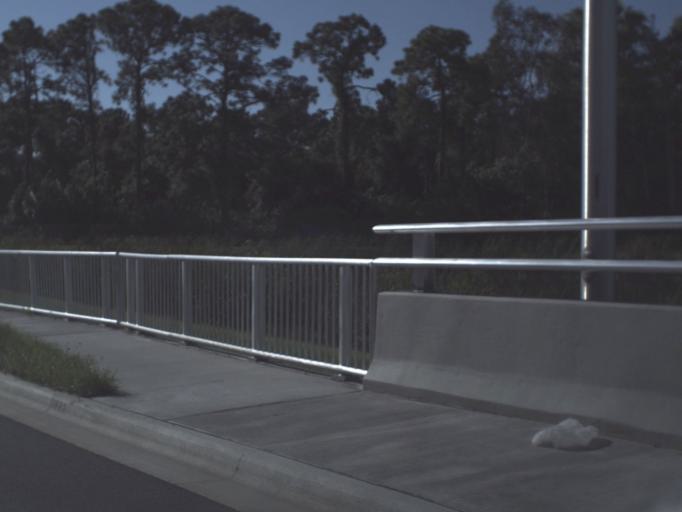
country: US
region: Florida
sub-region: Lee County
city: Fort Myers
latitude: 26.6109
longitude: -81.8534
